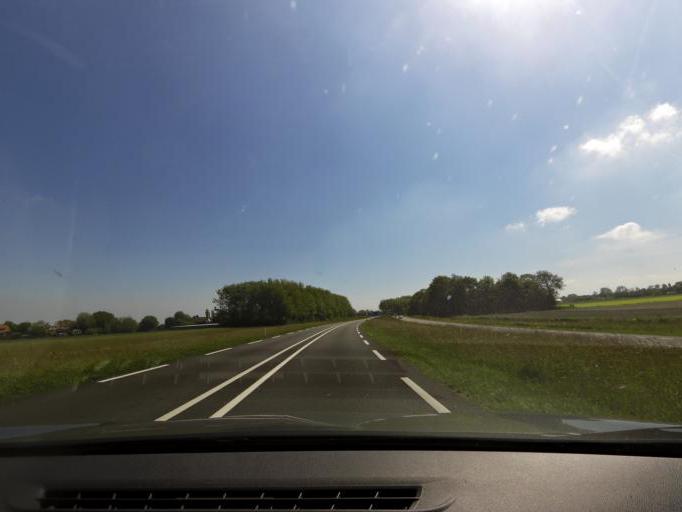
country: NL
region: South Holland
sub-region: Gemeente Hellevoetsluis
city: Nieuw-Helvoet
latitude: 51.8430
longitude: 4.0960
